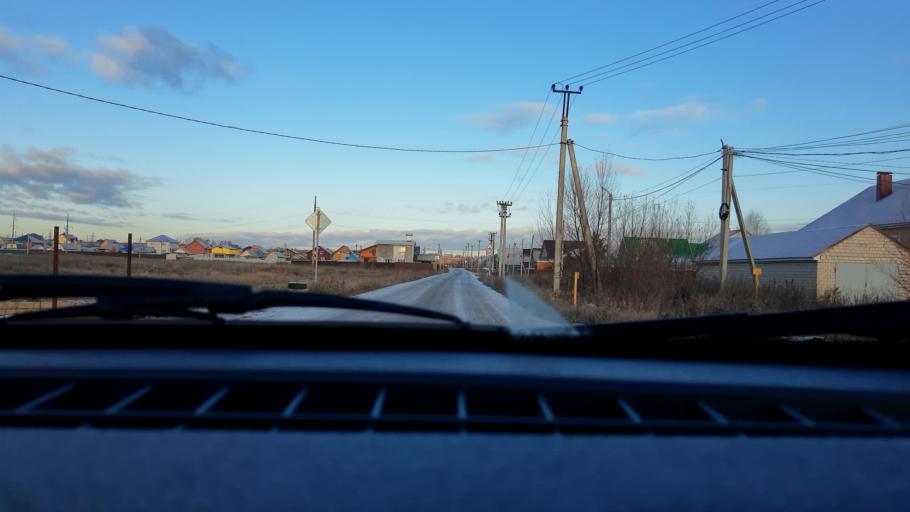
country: RU
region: Bashkortostan
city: Mikhaylovka
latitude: 54.7874
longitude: 55.8286
